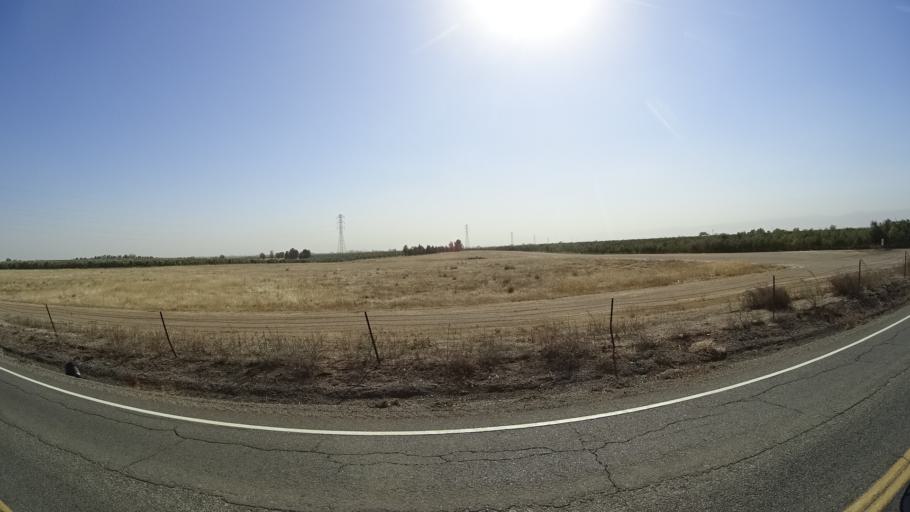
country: US
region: California
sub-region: Yolo County
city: Cottonwood
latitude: 38.7108
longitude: -121.8957
